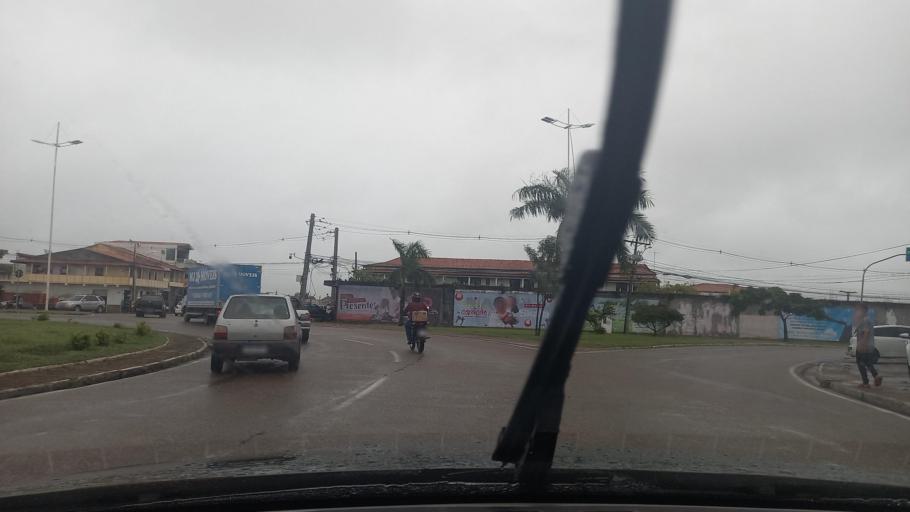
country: BR
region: Bahia
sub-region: Paulo Afonso
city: Paulo Afonso
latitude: -9.3995
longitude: -38.2325
